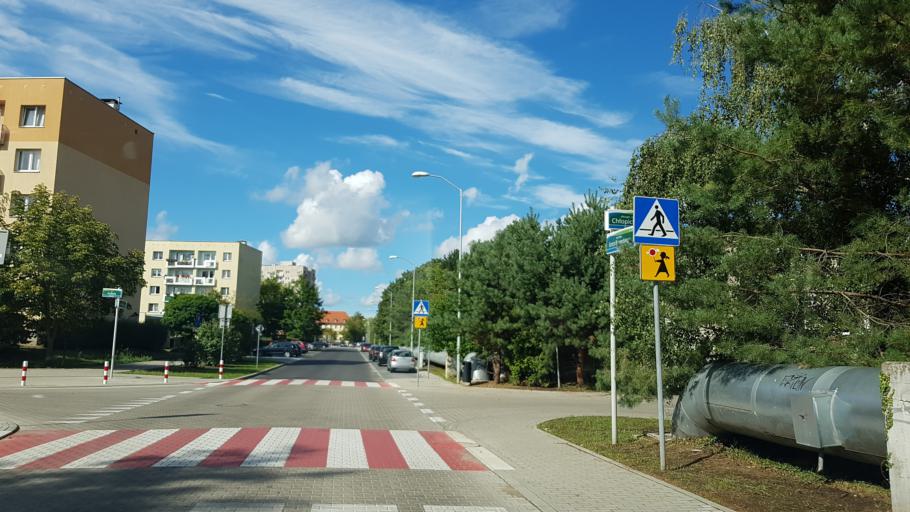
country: PL
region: West Pomeranian Voivodeship
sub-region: Szczecin
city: Szczecin
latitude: 53.4388
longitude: 14.4962
